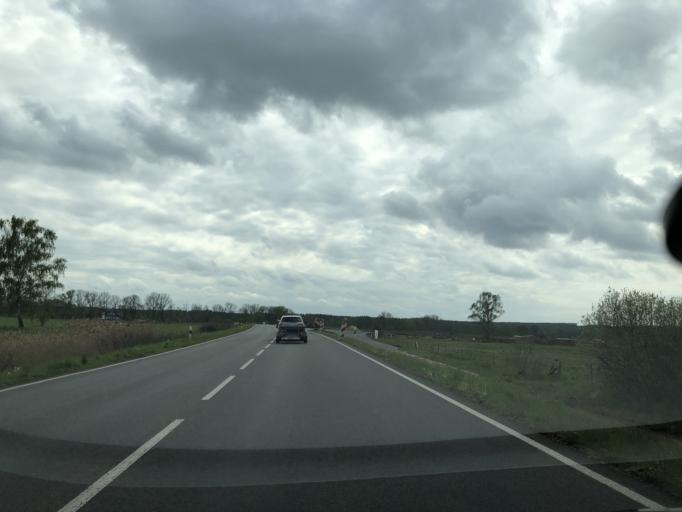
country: DE
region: Saxony-Anhalt
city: Luderitz
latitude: 52.5072
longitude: 11.7329
